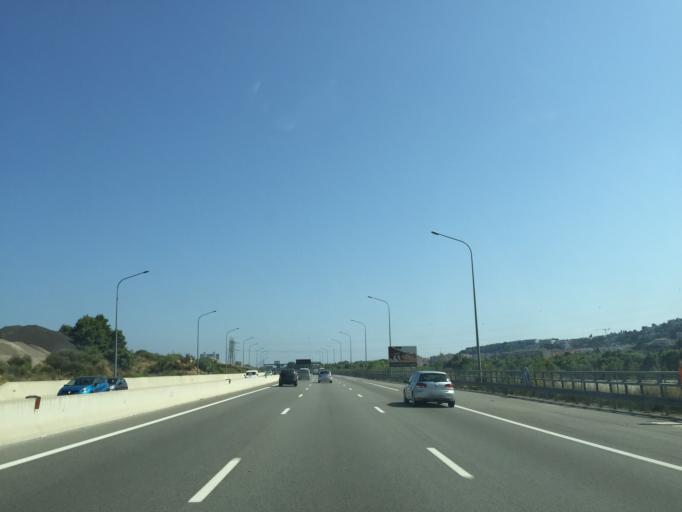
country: FR
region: Provence-Alpes-Cote d'Azur
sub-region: Departement des Alpes-Maritimes
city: Saint-Laurent-du-Var
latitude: 43.6898
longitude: 7.1899
